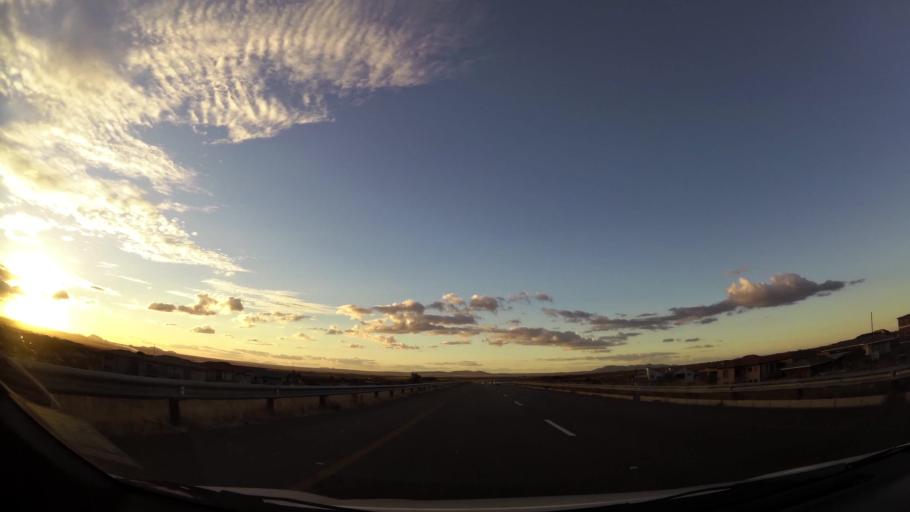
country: ZA
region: Limpopo
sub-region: Capricorn District Municipality
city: Polokwane
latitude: -23.8612
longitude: 29.5063
